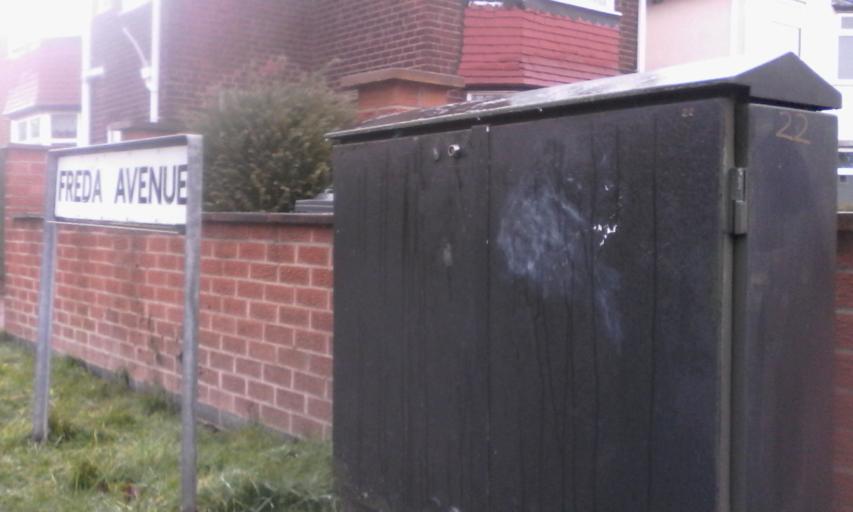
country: GB
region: England
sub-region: Nottinghamshire
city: Arnold
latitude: 52.9792
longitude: -1.0988
